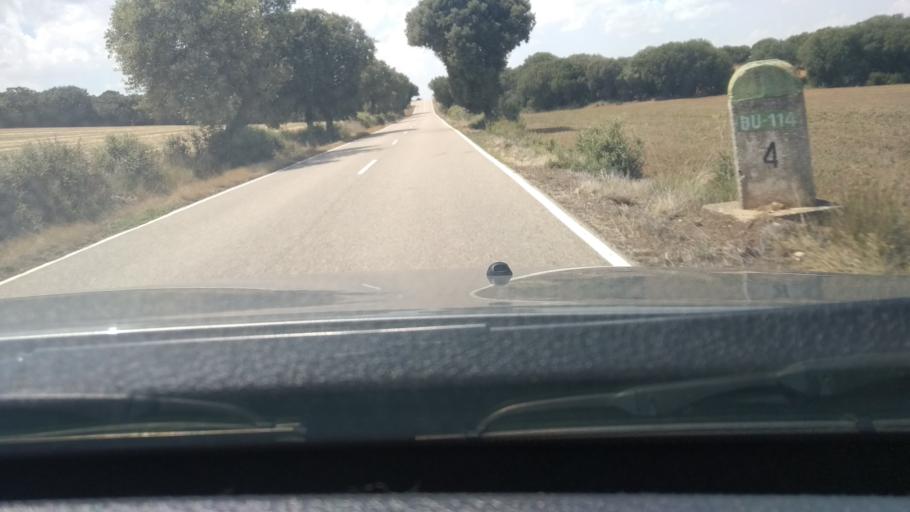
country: ES
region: Castille and Leon
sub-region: Provincia de Burgos
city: Avellanosa de Muno
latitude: 41.9777
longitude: -3.7988
